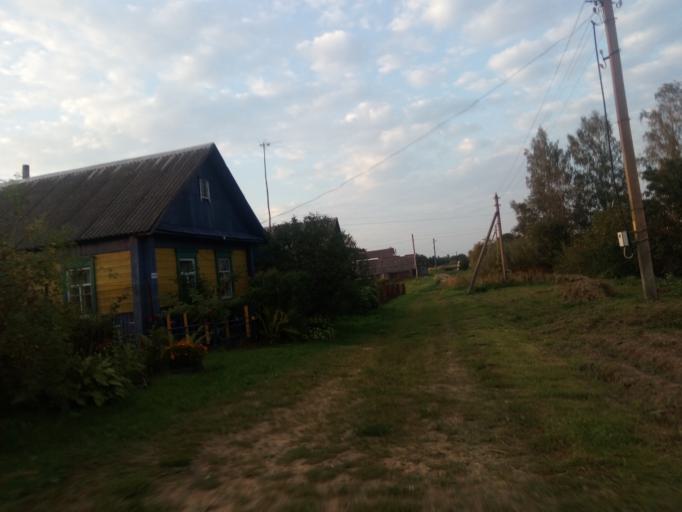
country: BY
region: Vitebsk
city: Dzisna
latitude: 55.6595
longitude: 28.3313
